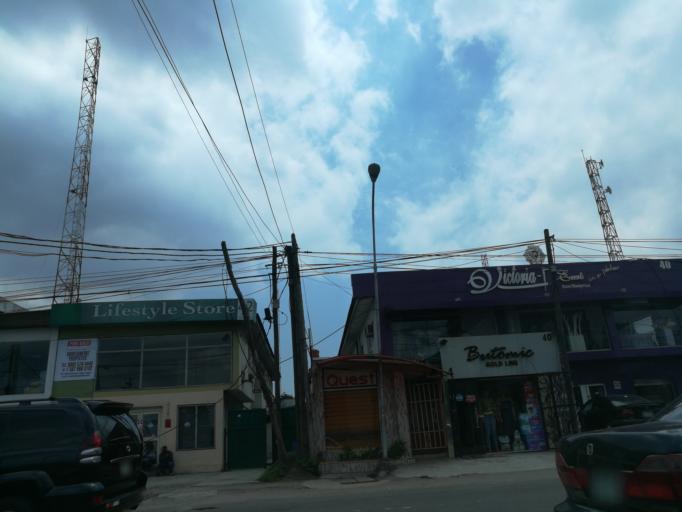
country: NG
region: Lagos
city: Ikeja
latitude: 6.6000
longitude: 3.3527
